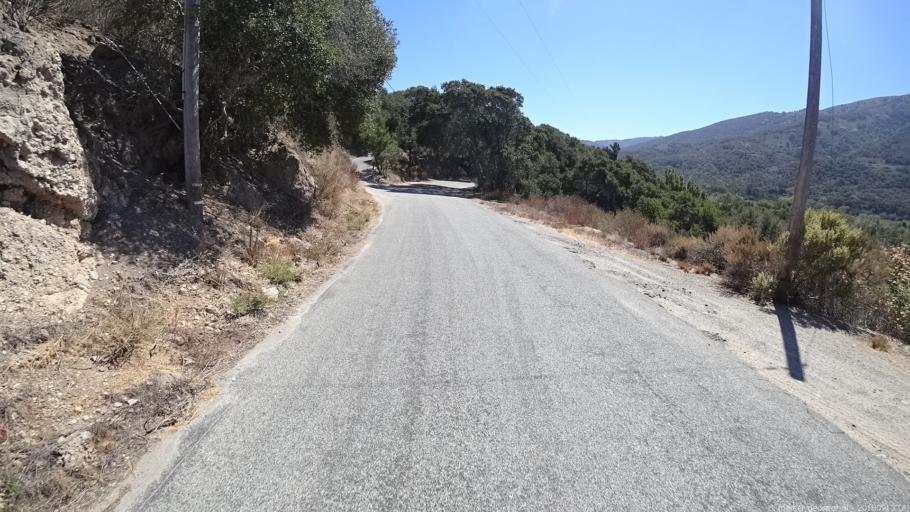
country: US
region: California
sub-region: Monterey County
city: Carmel Valley Village
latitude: 36.5137
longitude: -121.7696
